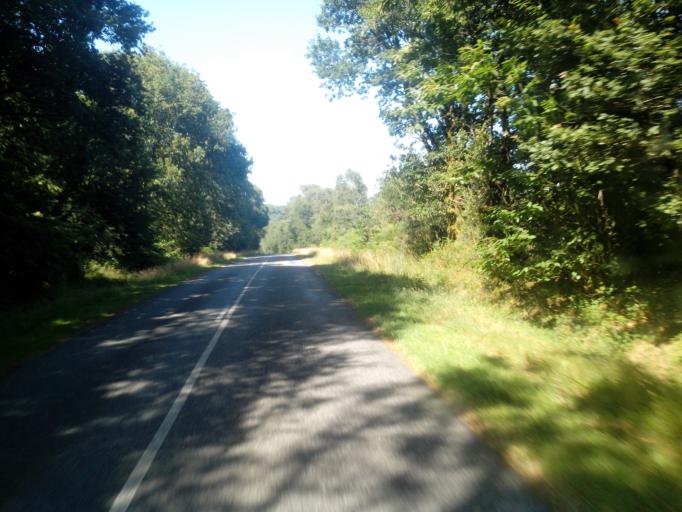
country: FR
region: Brittany
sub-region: Departement du Morbihan
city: Campeneac
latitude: 47.9933
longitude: -2.2526
